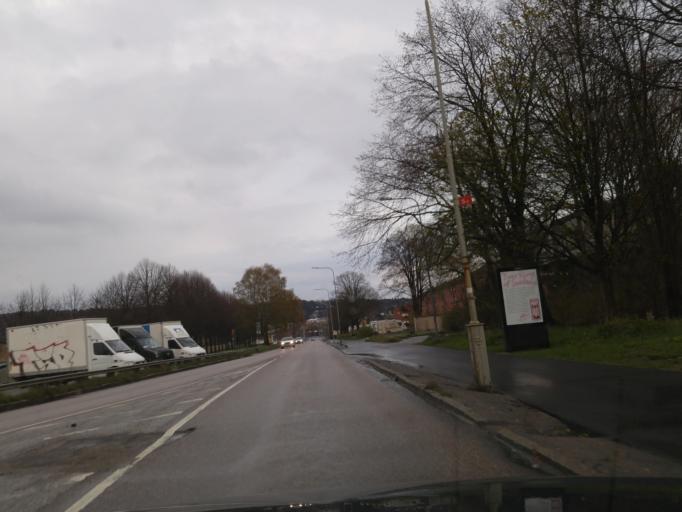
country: SE
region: Vaestra Goetaland
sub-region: Goteborg
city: Majorna
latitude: 57.6600
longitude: 11.9256
